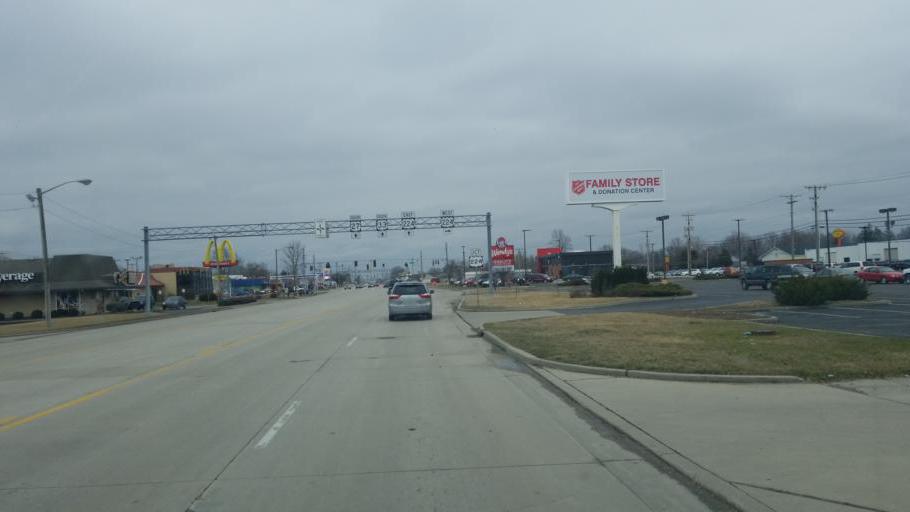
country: US
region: Indiana
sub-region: Adams County
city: Decatur
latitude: 40.8343
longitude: -84.9378
